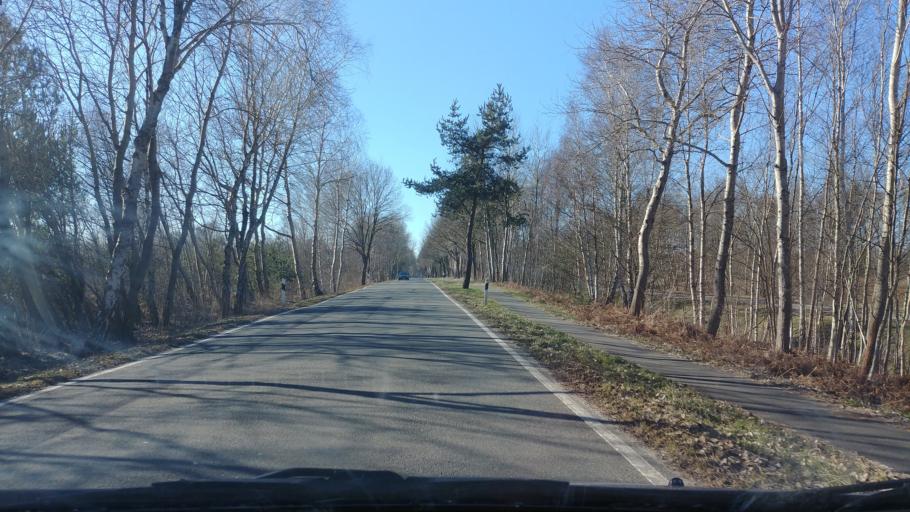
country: DE
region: Lower Saxony
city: Neustadt am Rubenberge
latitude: 52.5051
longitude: 9.4131
